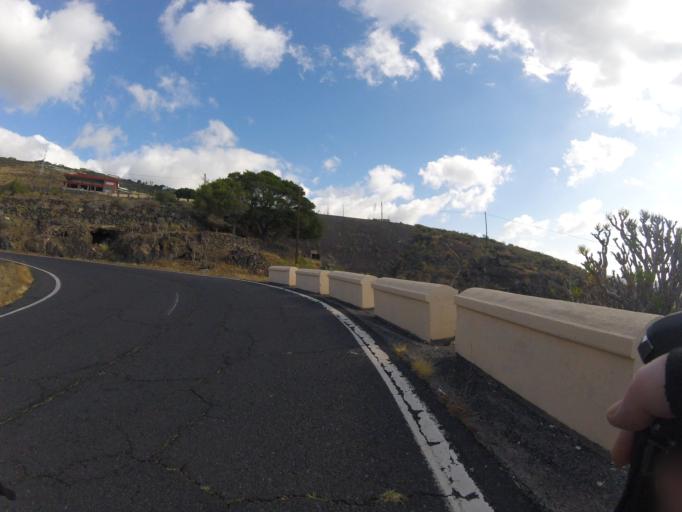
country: ES
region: Canary Islands
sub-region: Provincia de Santa Cruz de Tenerife
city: Candelaria
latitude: 28.3899
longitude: -16.3523
